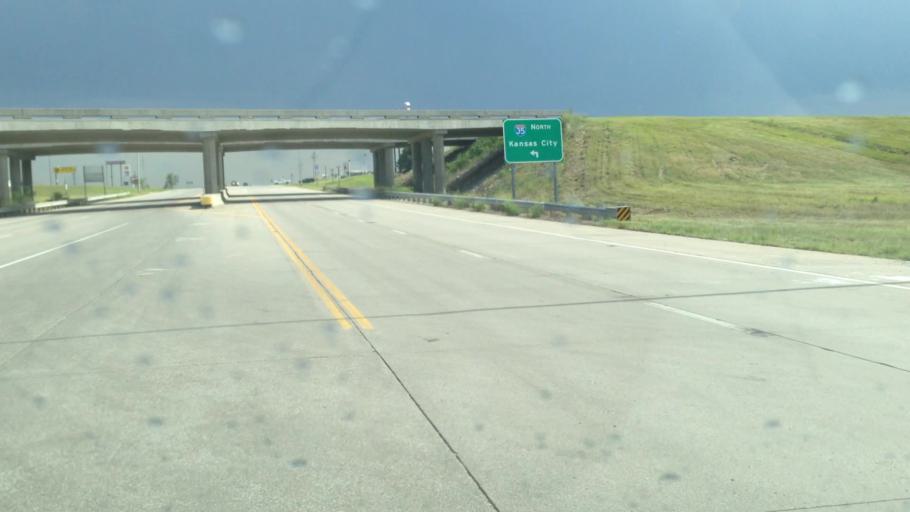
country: US
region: Kansas
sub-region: Osage County
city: Lyndon
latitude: 38.4300
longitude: -95.7286
